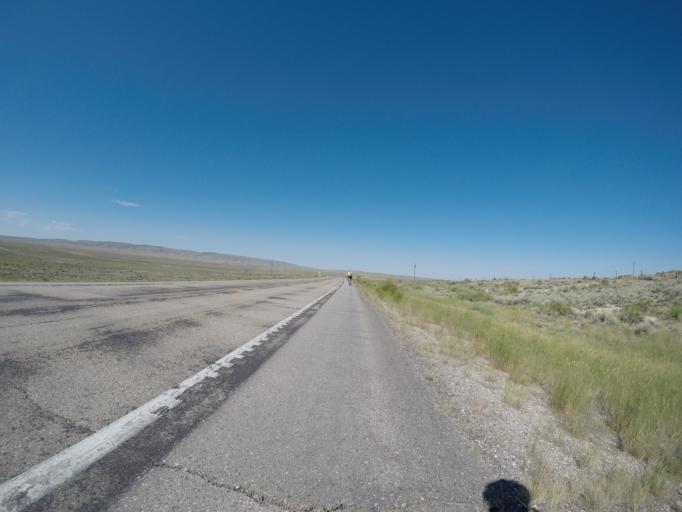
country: US
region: Wyoming
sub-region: Carbon County
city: Saratoga
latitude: 41.8252
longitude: -106.6428
